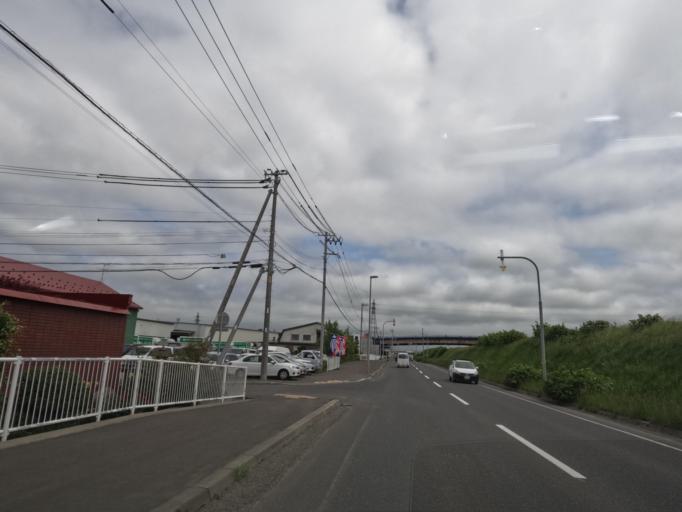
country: JP
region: Hokkaido
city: Sapporo
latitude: 43.0809
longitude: 141.4102
